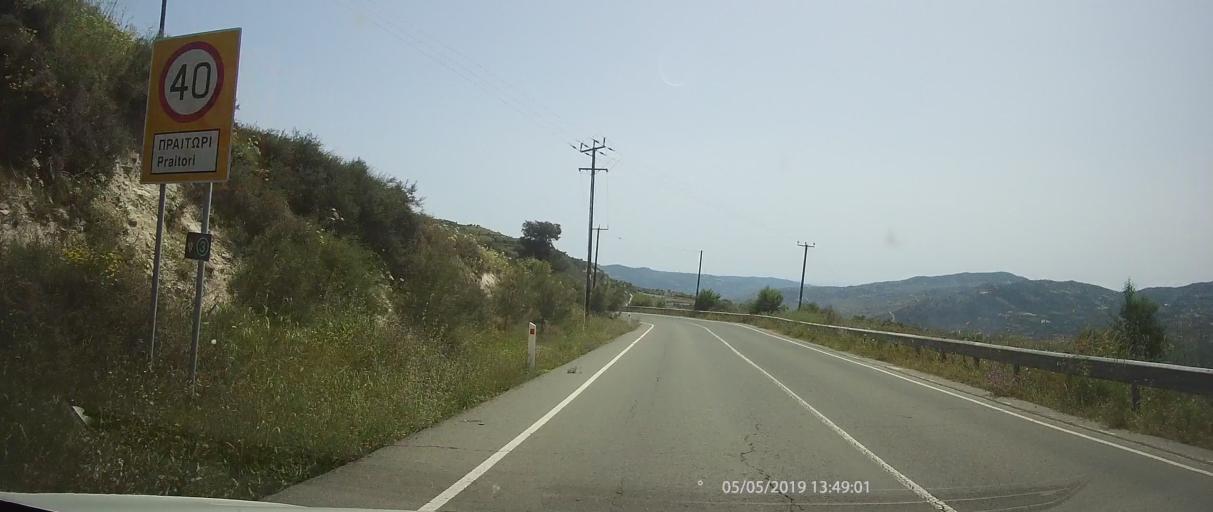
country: CY
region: Limassol
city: Pachna
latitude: 34.8523
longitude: 32.7489
